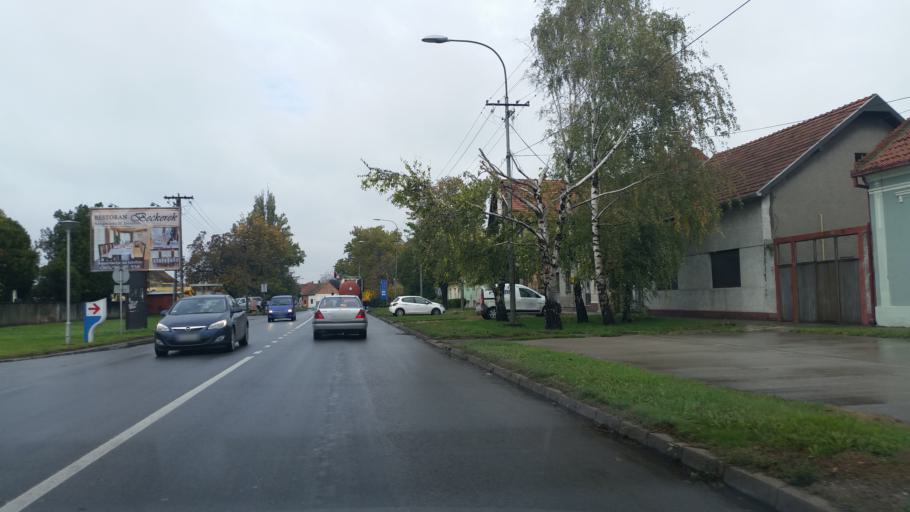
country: RS
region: Autonomna Pokrajina Vojvodina
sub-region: Srednjebanatski Okrug
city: Zrenjanin
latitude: 45.3758
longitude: 20.4101
